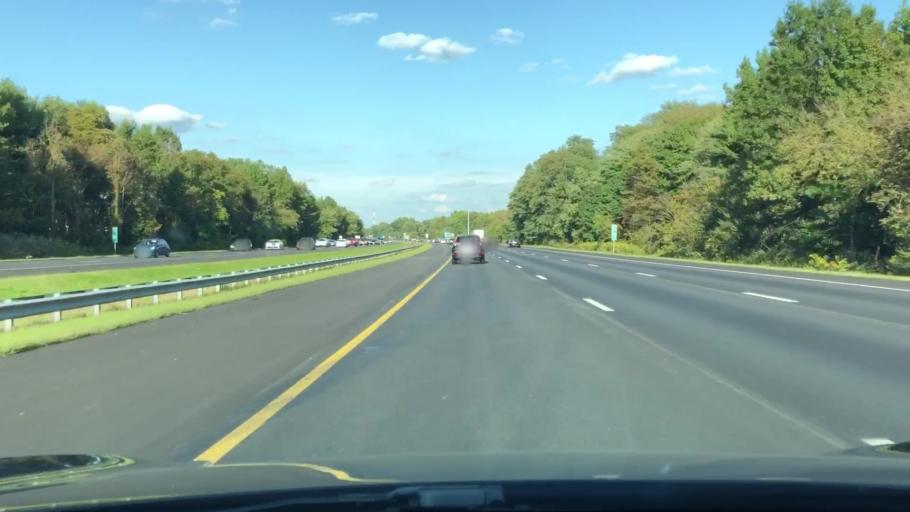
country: US
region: New Jersey
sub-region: Burlington County
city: Ramblewood
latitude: 39.9458
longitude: -74.9371
